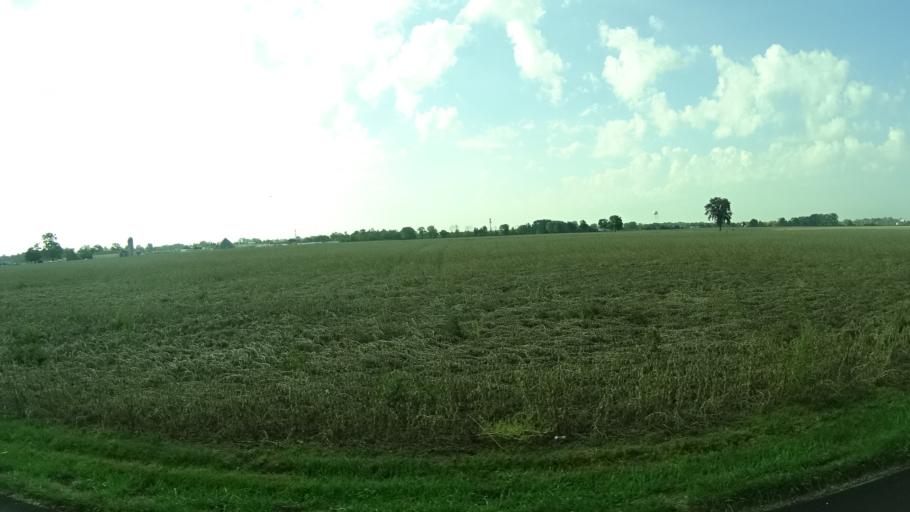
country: US
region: Indiana
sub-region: Madison County
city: Ingalls
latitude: 40.0024
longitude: -85.8463
